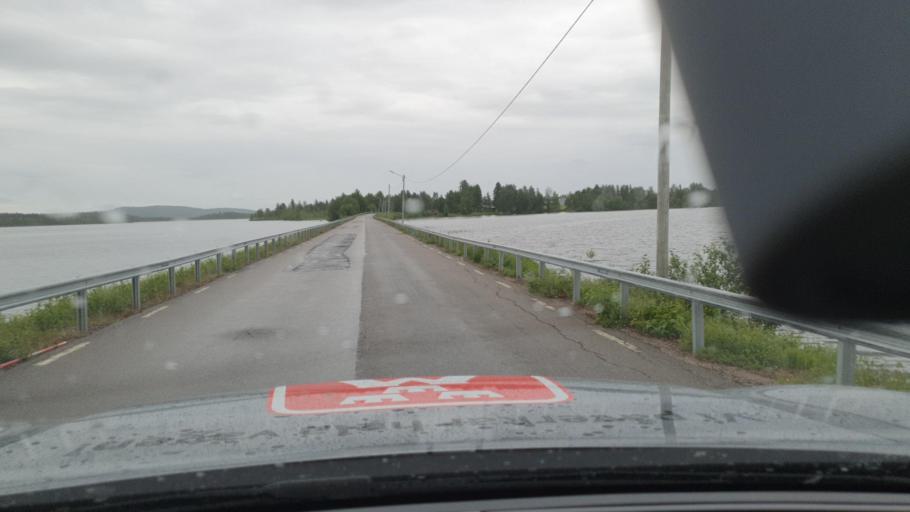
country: SE
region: Norrbotten
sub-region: Pajala Kommun
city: Pajala
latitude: 66.8029
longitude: 23.1210
